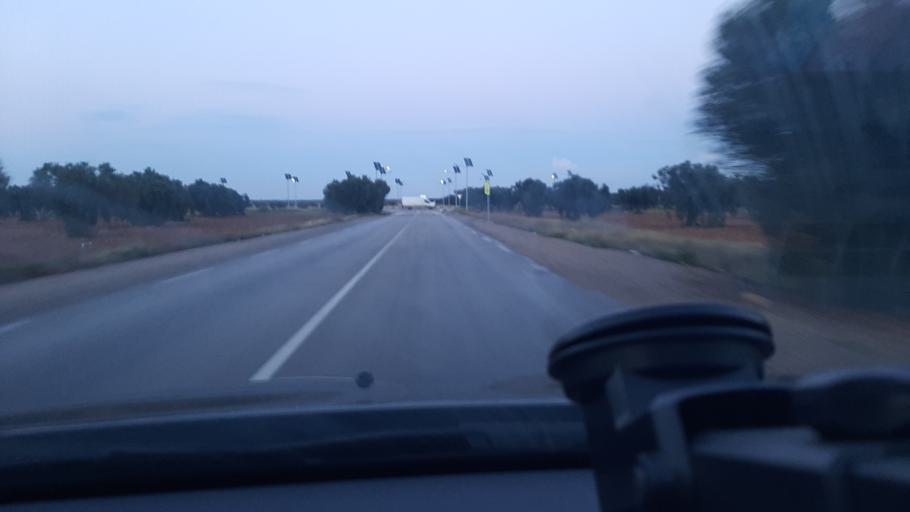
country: TN
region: Al Mahdiyah
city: Shurban
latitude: 35.0386
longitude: 10.5238
